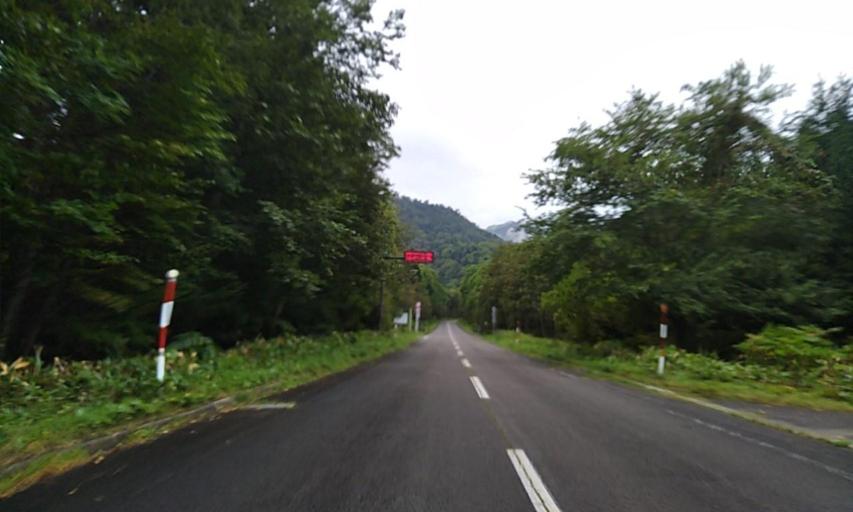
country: JP
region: Hokkaido
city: Bihoro
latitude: 43.5842
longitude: 144.2670
